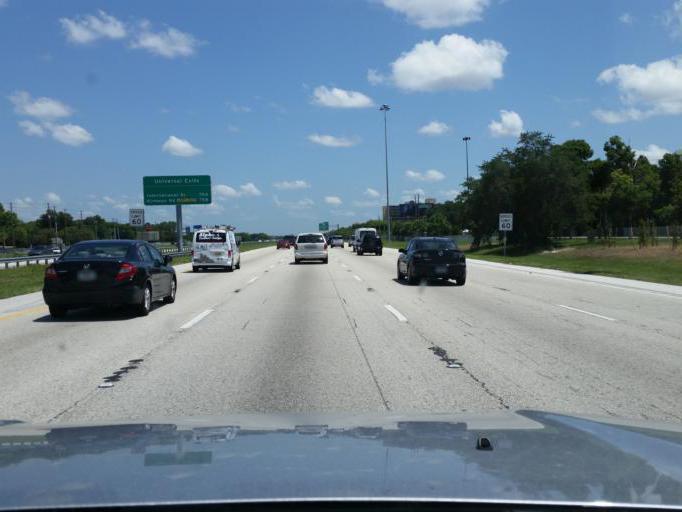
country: US
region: Florida
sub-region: Orange County
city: Doctor Phillips
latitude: 28.4261
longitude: -81.4741
